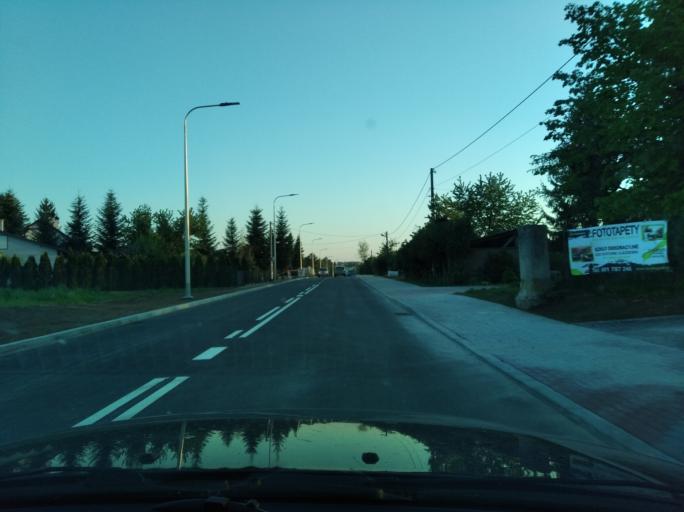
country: PL
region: Subcarpathian Voivodeship
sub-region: Powiat rzeszowski
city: Tyczyn
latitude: 50.0127
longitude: 22.0394
